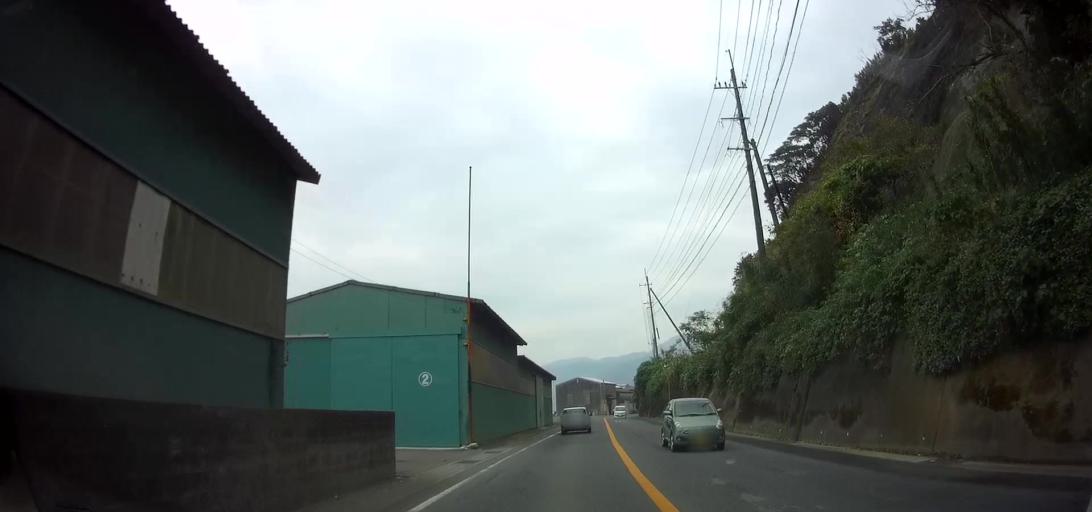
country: JP
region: Nagasaki
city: Shimabara
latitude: 32.7141
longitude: 130.1894
